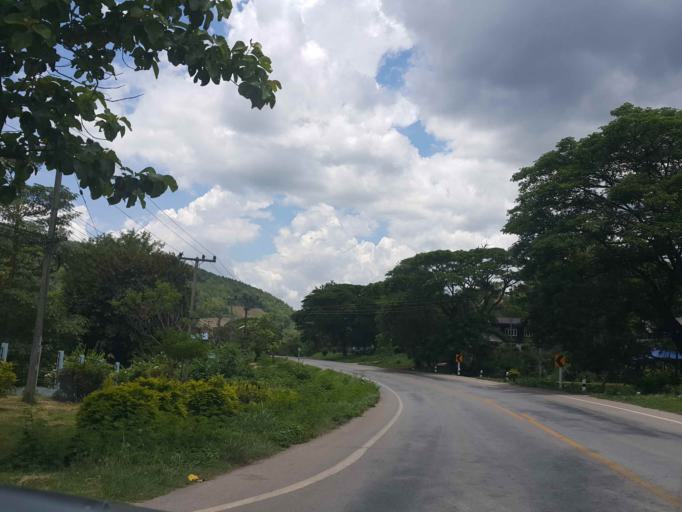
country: TH
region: Nan
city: Wiang Sa
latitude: 18.5240
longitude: 100.5664
